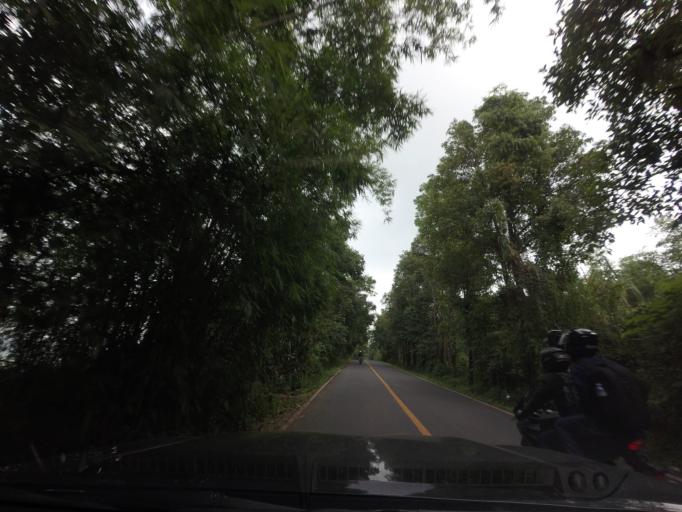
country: TH
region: Nan
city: Bo Kluea
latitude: 19.1892
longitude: 101.0428
